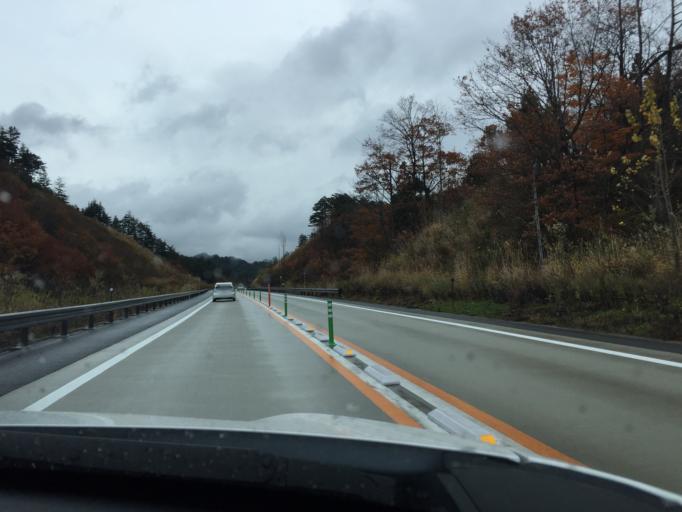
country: JP
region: Yamagata
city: Yonezawa
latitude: 37.8820
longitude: 140.1781
